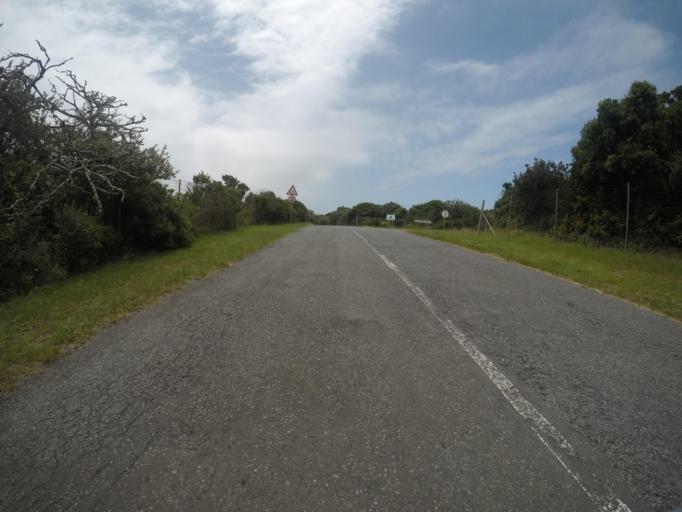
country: ZA
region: Eastern Cape
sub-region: Buffalo City Metropolitan Municipality
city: East London
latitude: -32.9943
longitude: 27.9413
